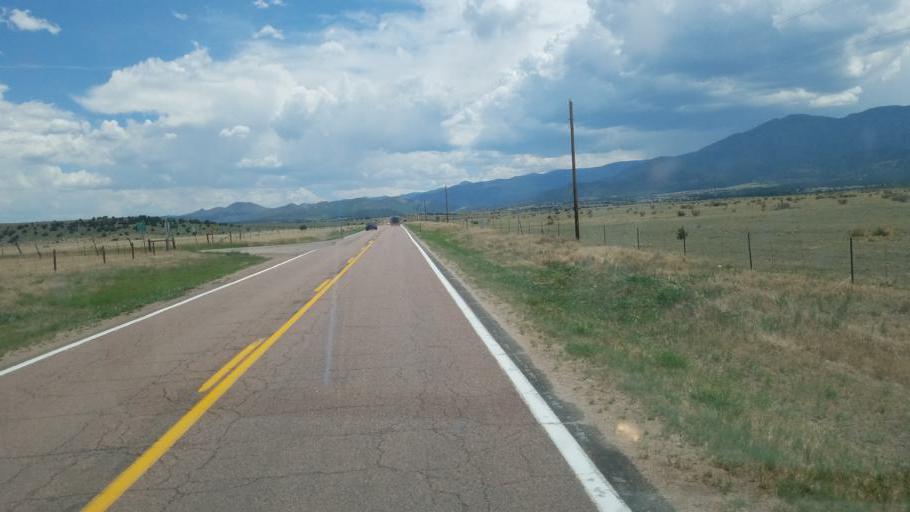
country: US
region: Colorado
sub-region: Fremont County
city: Florence
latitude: 38.2877
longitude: -105.0874
